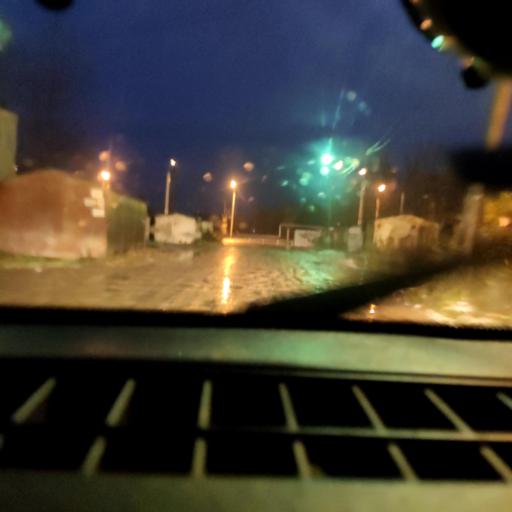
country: RU
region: Bashkortostan
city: Ufa
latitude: 54.8066
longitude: 56.1502
